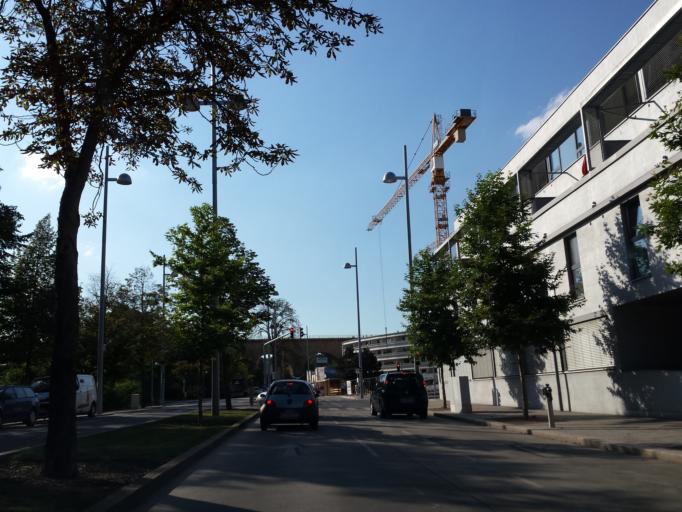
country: AT
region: Lower Austria
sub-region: Politischer Bezirk Modling
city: Perchtoldsdorf
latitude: 48.1377
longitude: 16.2762
